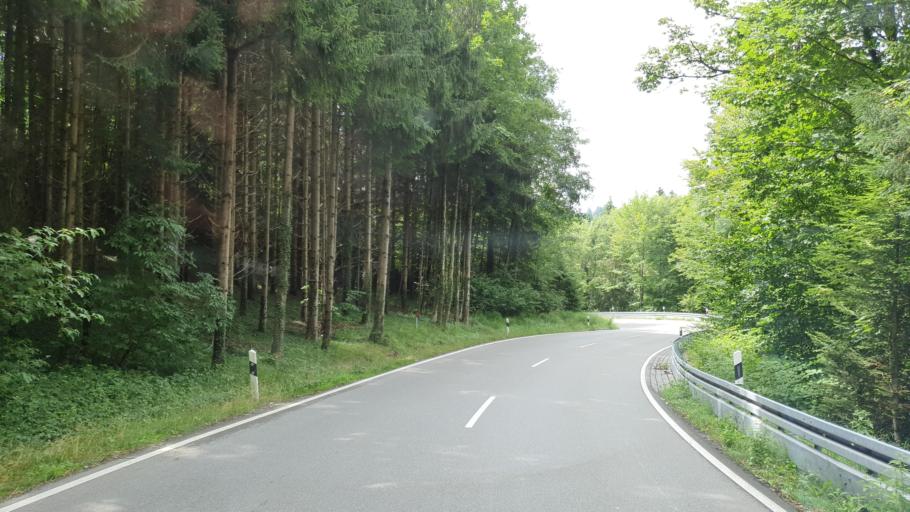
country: AT
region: Vorarlberg
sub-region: Politischer Bezirk Bregenz
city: Moggers
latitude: 47.5937
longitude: 9.8159
